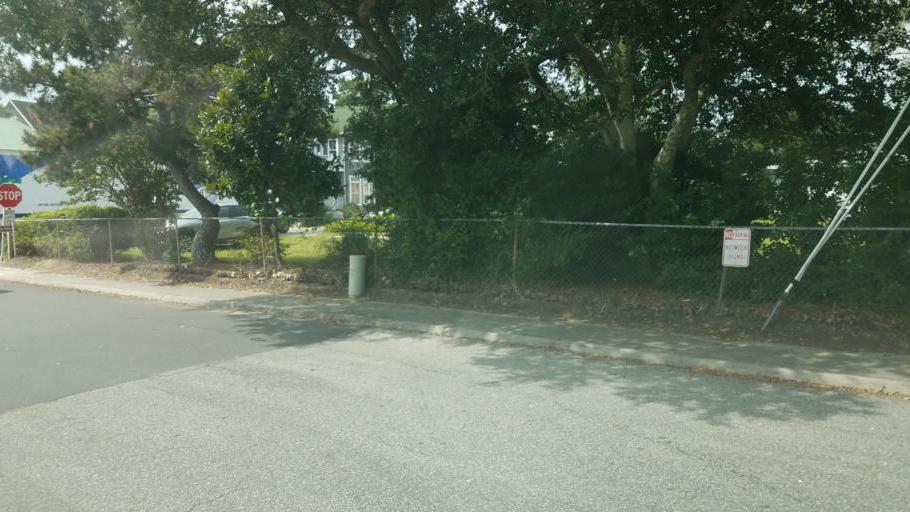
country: US
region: North Carolina
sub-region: Dare County
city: Manteo
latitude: 35.9109
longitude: -75.6700
